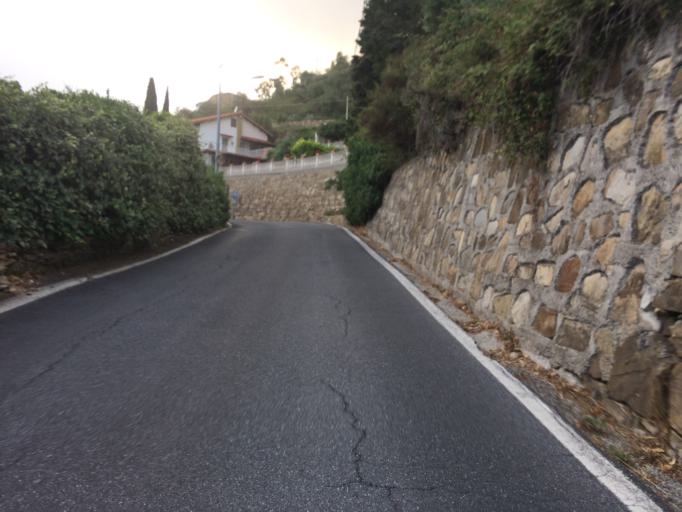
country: IT
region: Liguria
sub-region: Provincia di Imperia
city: San Remo
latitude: 43.8435
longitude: 7.7437
